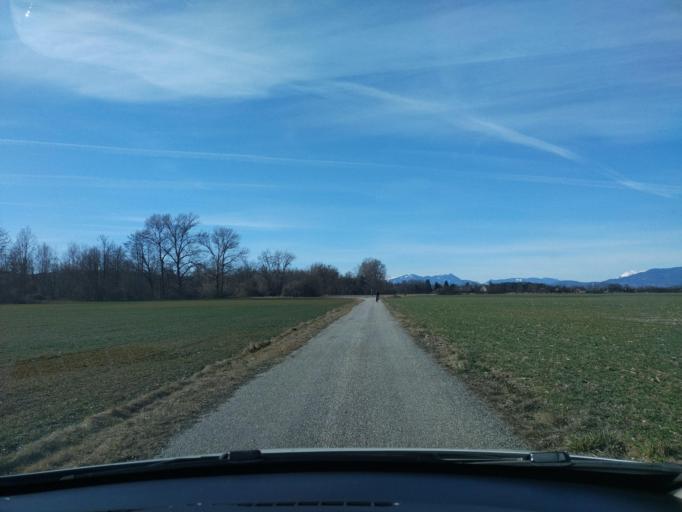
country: AT
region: Lower Austria
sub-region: Politischer Bezirk Neunkirchen
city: Pitten
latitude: 47.7374
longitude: 16.1914
